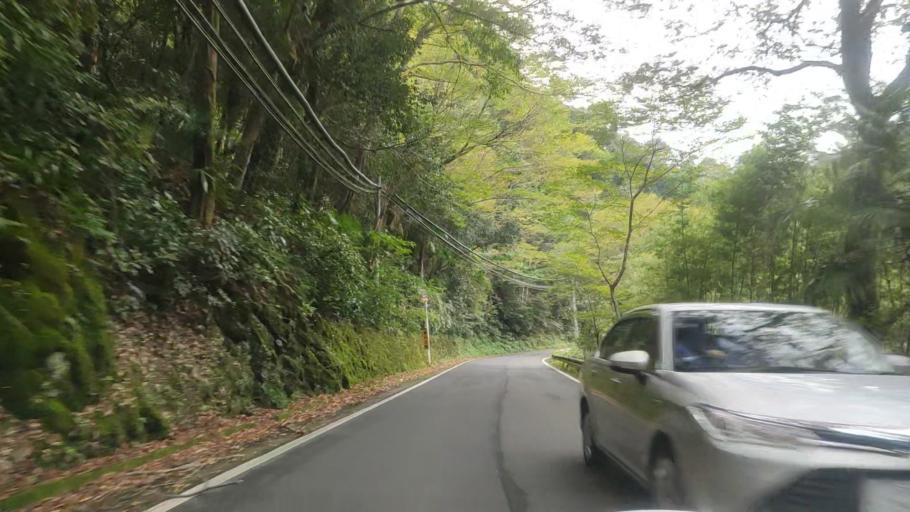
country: JP
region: Wakayama
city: Hashimoto
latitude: 34.2722
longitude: 135.5613
